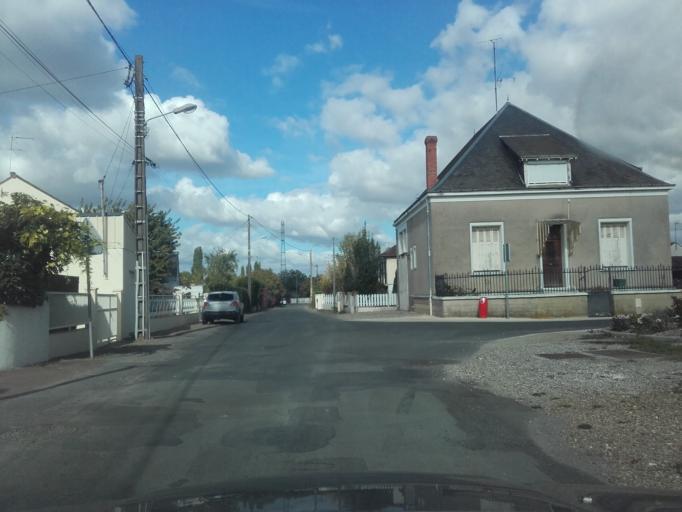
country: FR
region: Centre
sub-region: Departement d'Indre-et-Loire
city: La Ville-aux-Dames
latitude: 47.3957
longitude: 0.7570
